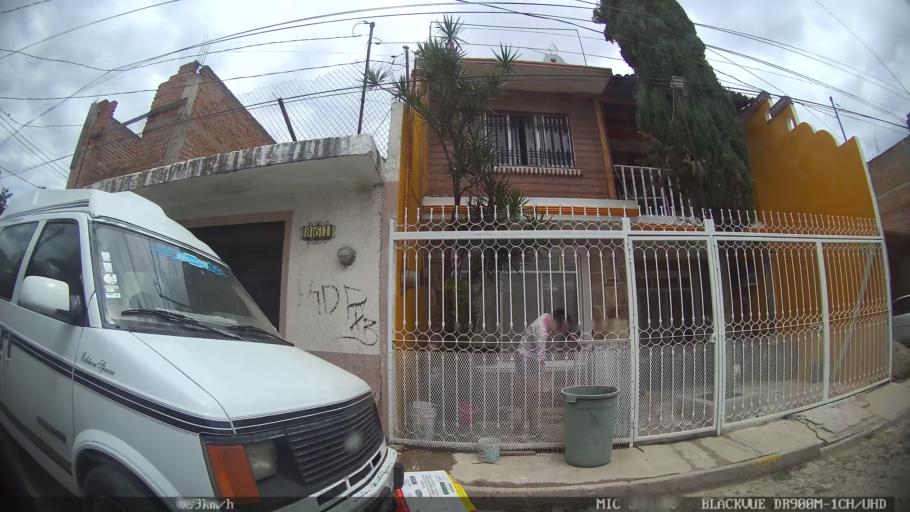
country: MX
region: Jalisco
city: Tonala
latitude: 20.6435
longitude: -103.2503
